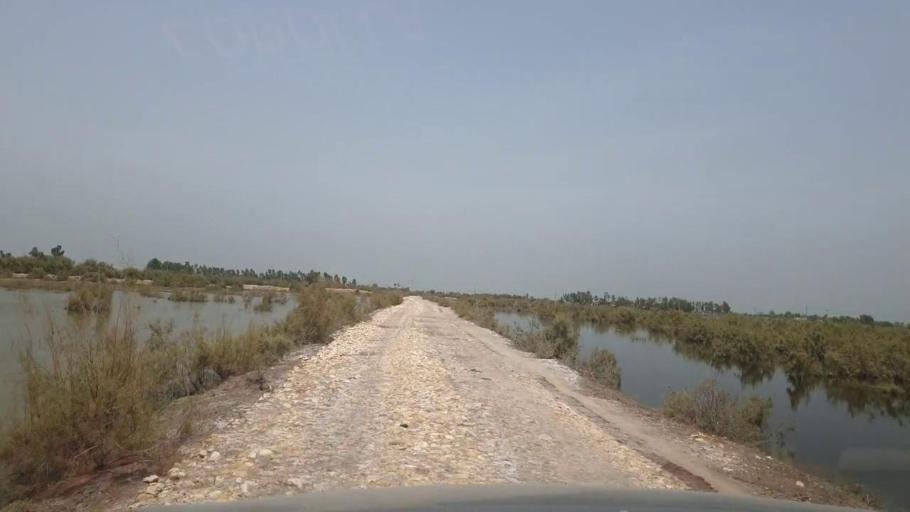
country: PK
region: Sindh
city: Garhi Yasin
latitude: 27.9163
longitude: 68.4151
